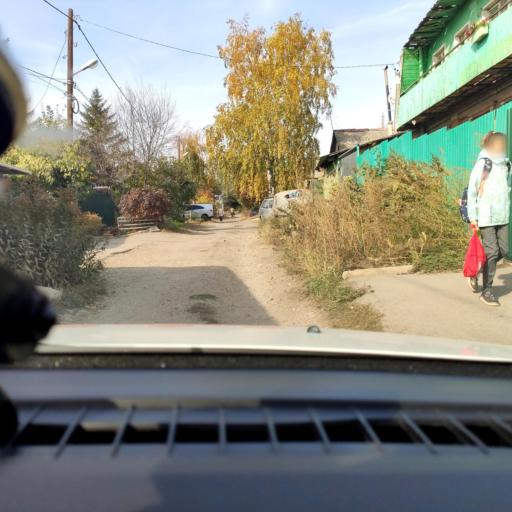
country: RU
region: Samara
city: Samara
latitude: 53.1832
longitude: 50.1791
